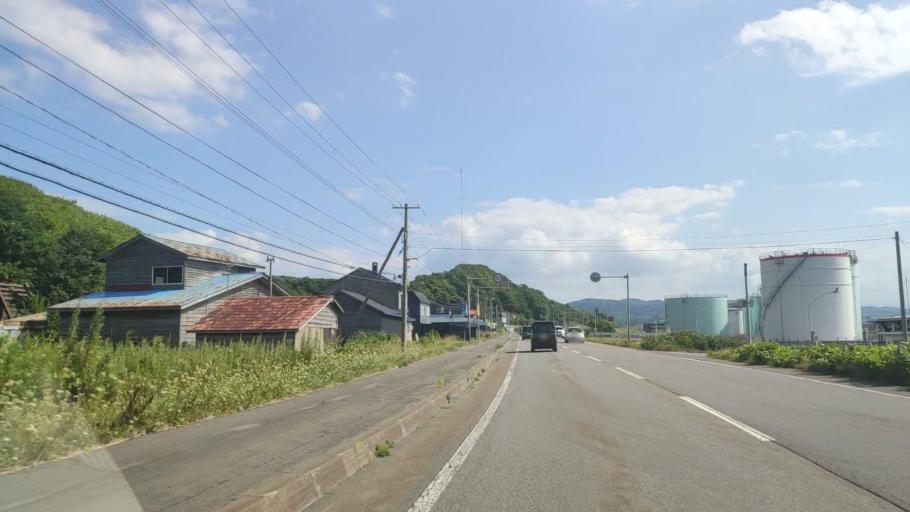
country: JP
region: Hokkaido
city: Rumoi
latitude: 43.9605
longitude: 141.6431
